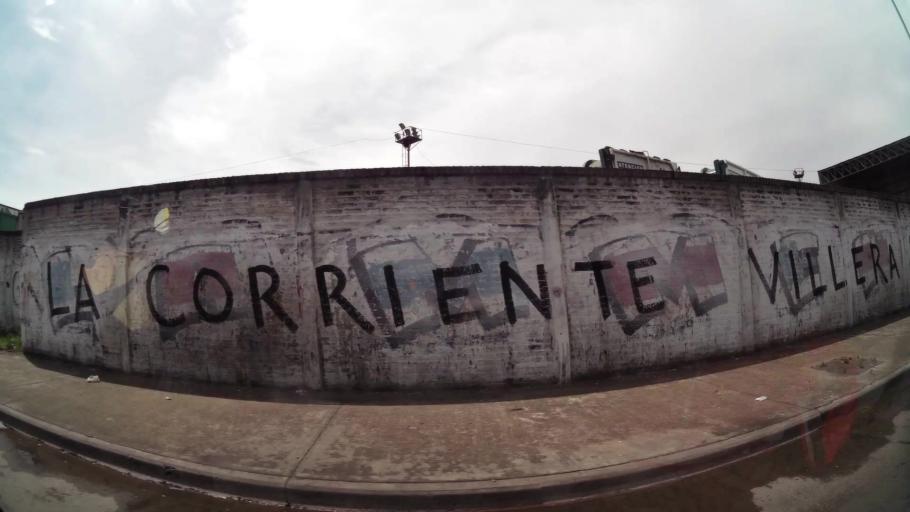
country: AR
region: Buenos Aires F.D.
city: Villa Lugano
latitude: -34.6507
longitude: -58.4553
